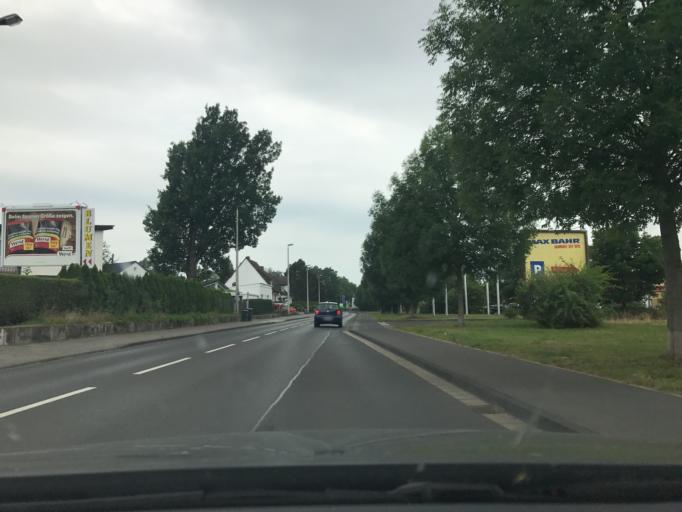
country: DE
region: Hesse
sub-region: Regierungsbezirk Kassel
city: Lohfelden
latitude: 51.3067
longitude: 9.5433
